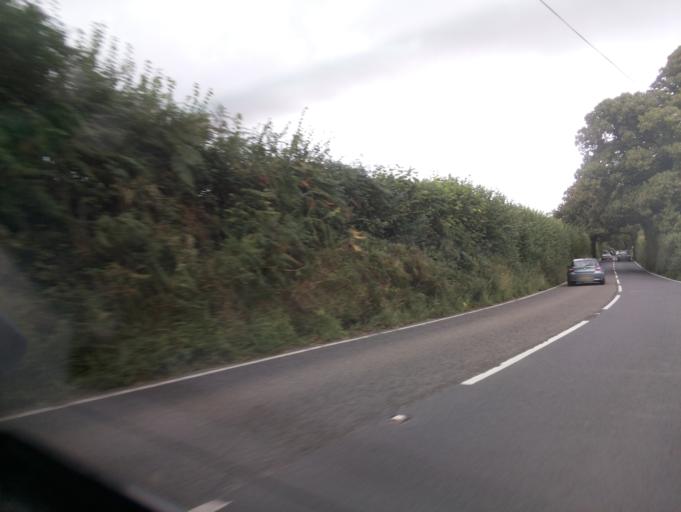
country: GB
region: England
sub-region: Devon
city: Exminster
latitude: 50.6678
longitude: -3.4829
